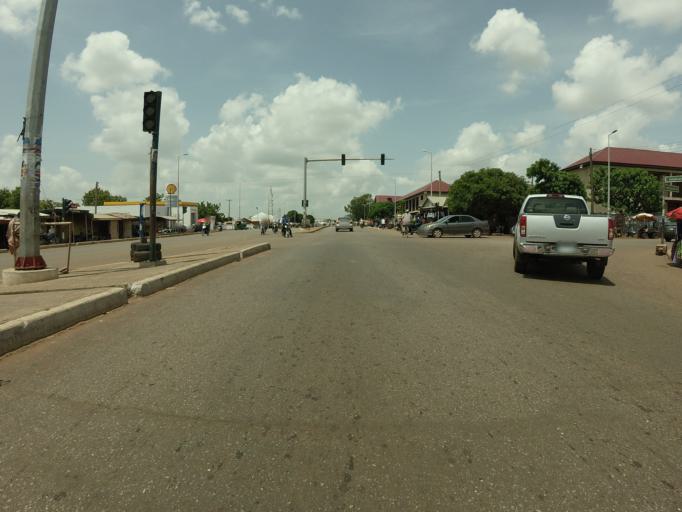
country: GH
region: Northern
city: Tamale
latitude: 9.4043
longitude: -0.8514
